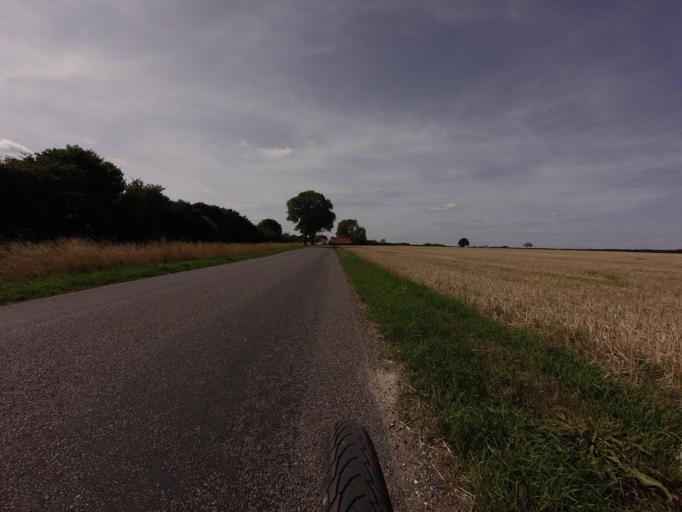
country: DK
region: Zealand
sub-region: Stevns Kommune
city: Store Heddinge
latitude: 55.2425
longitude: 12.3274
